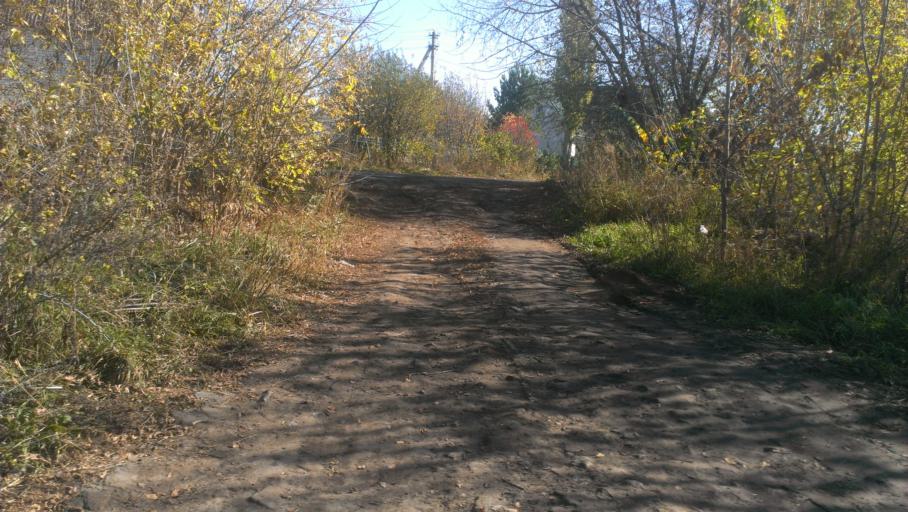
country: RU
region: Altai Krai
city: Novosilikatnyy
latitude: 53.3542
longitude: 83.6314
